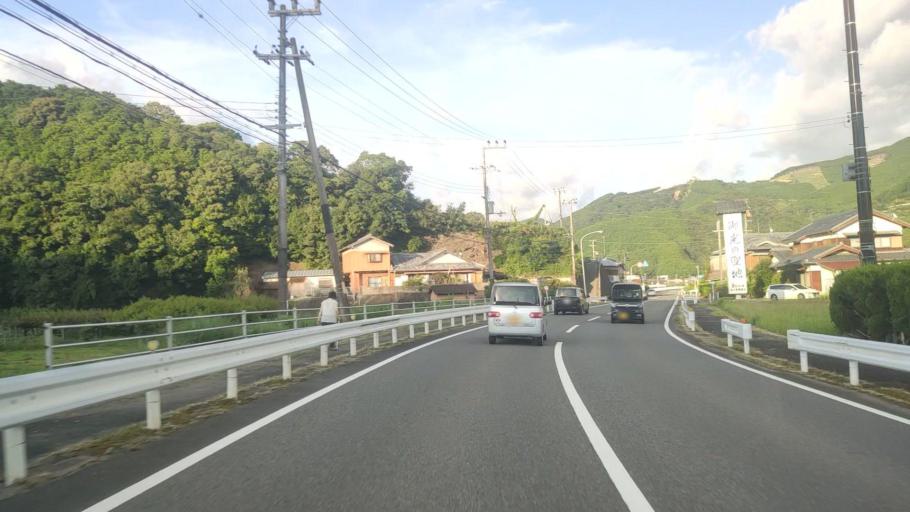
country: JP
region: Wakayama
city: Tanabe
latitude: 33.7186
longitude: 135.4729
